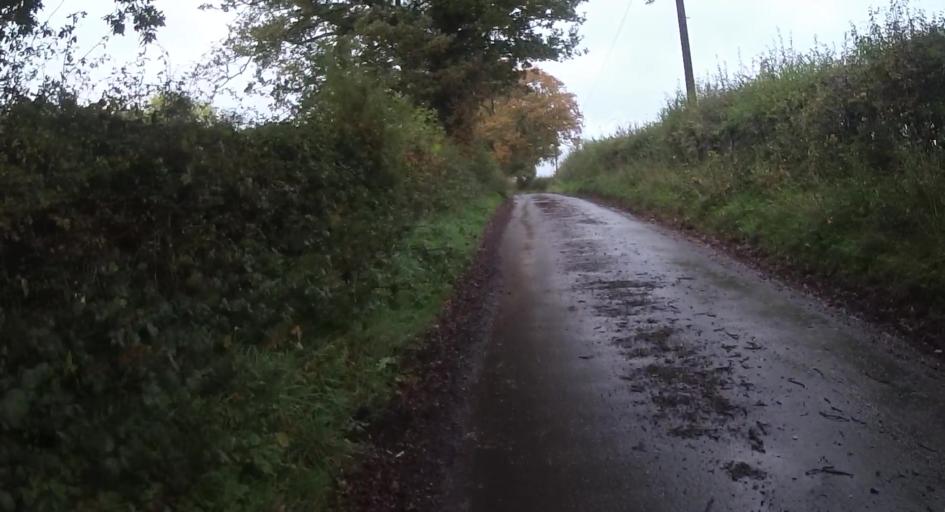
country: GB
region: England
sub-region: Surrey
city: Farnham
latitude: 51.2228
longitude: -0.8296
